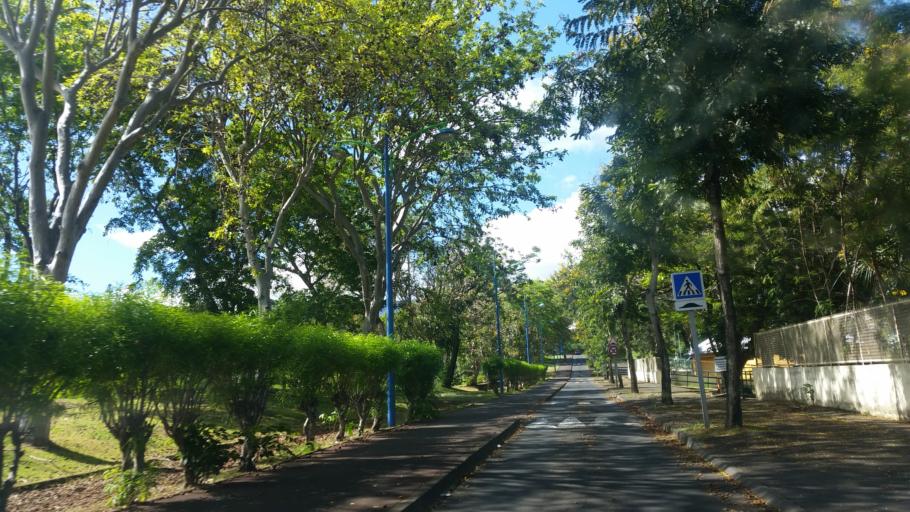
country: RE
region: Reunion
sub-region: Reunion
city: Saint-Denis
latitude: -20.8962
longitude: 55.4865
